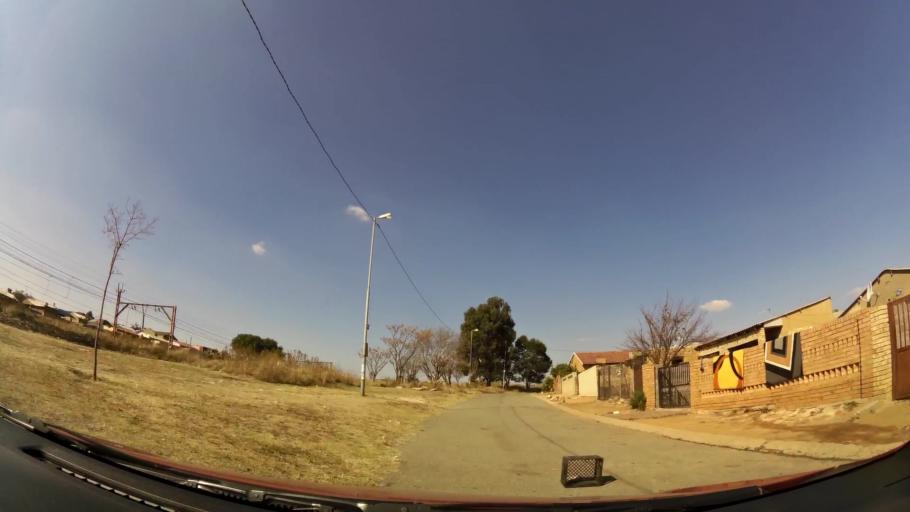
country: ZA
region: Gauteng
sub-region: City of Johannesburg Metropolitan Municipality
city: Soweto
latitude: -26.2261
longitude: 27.8871
